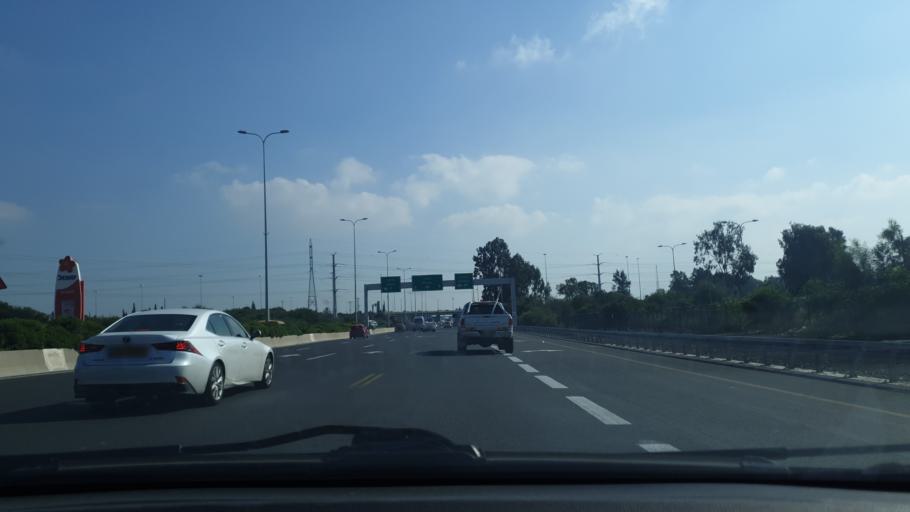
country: IL
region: Tel Aviv
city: Azor
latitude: 32.0147
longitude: 34.8112
